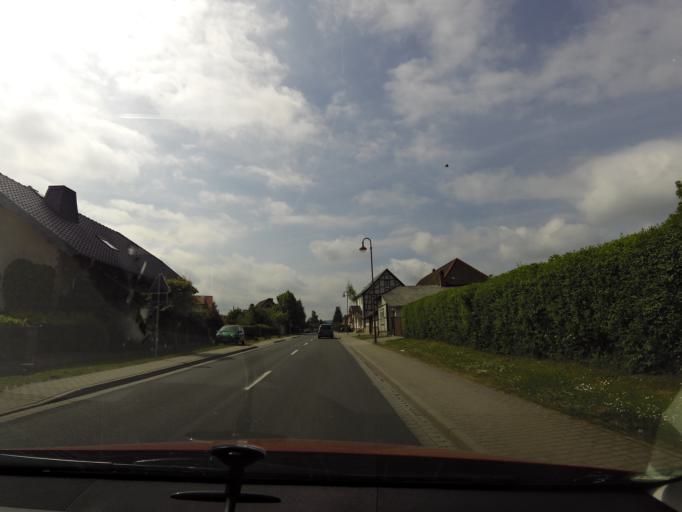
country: DE
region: Thuringia
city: Langula
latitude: 51.1506
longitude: 10.4140
